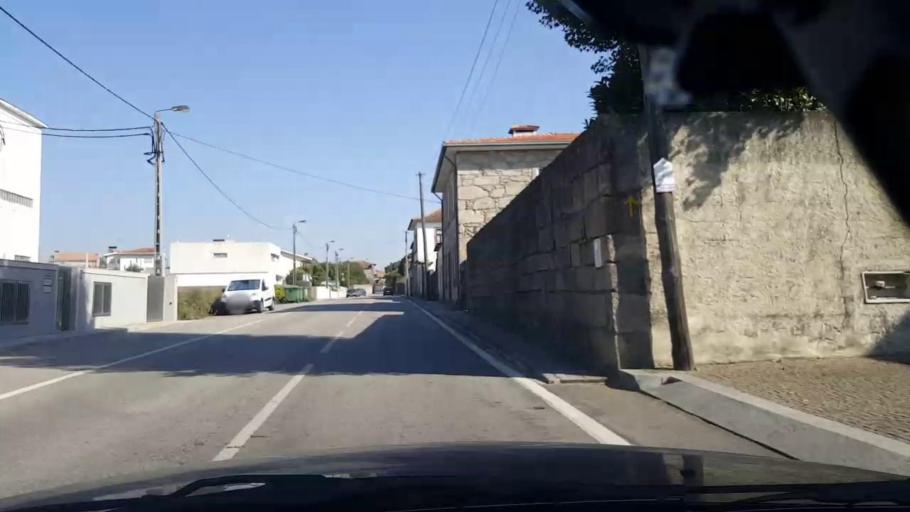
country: PT
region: Porto
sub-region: Maia
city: Gemunde
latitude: 41.3023
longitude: -8.6791
